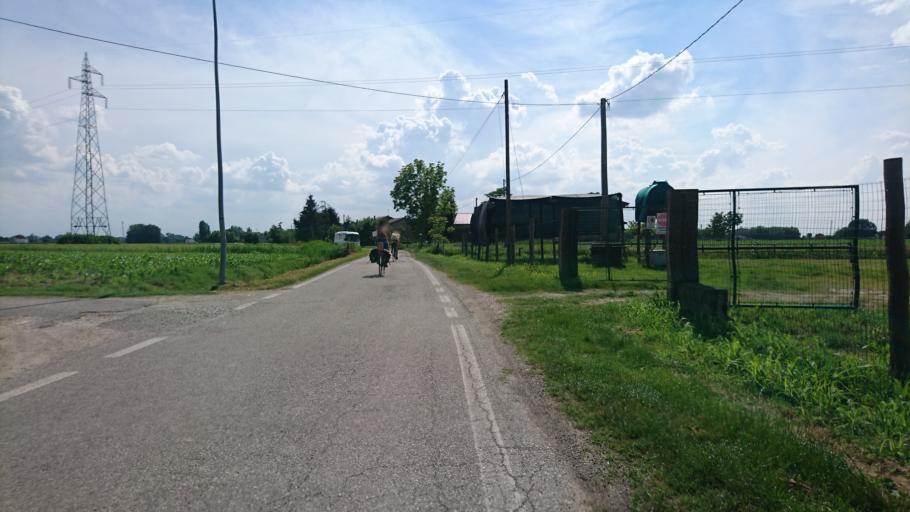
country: IT
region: Veneto
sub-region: Provincia di Rovigo
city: Castelmassa
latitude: 45.0349
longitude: 11.3097
